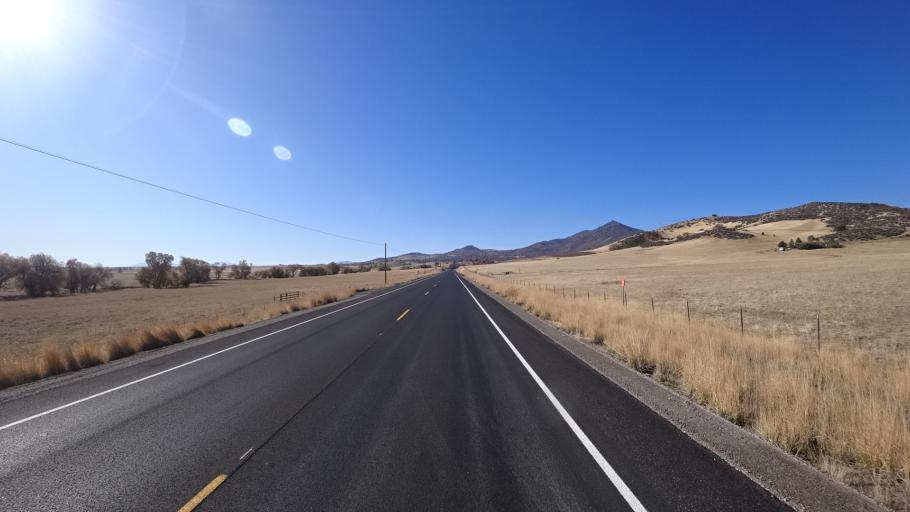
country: US
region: California
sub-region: Siskiyou County
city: Montague
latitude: 41.8339
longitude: -122.4869
